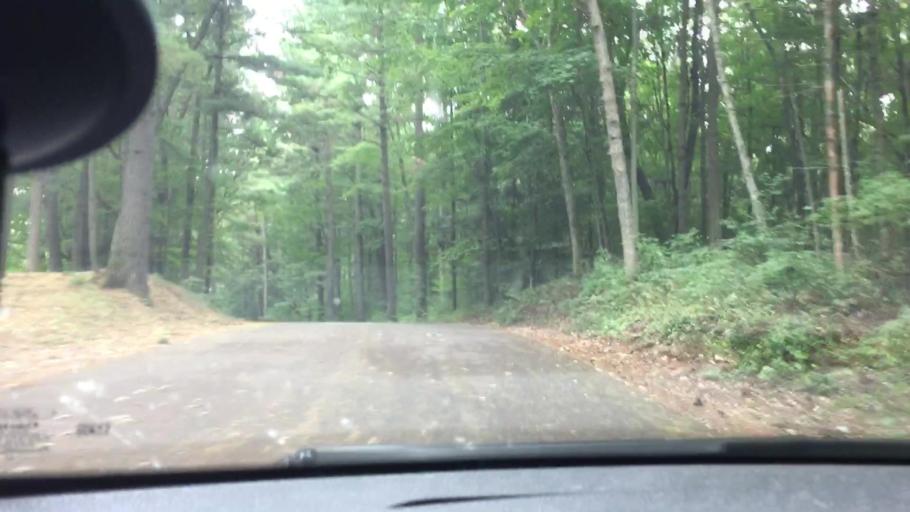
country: US
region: Wisconsin
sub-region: Chippewa County
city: Chippewa Falls
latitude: 44.9551
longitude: -91.4026
